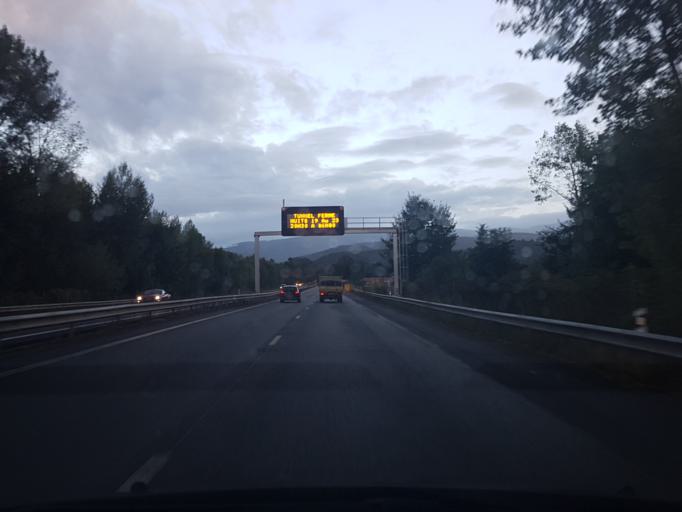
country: FR
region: Midi-Pyrenees
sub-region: Departement de l'Ariege
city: Varilhes
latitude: 43.0228
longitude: 1.6156
